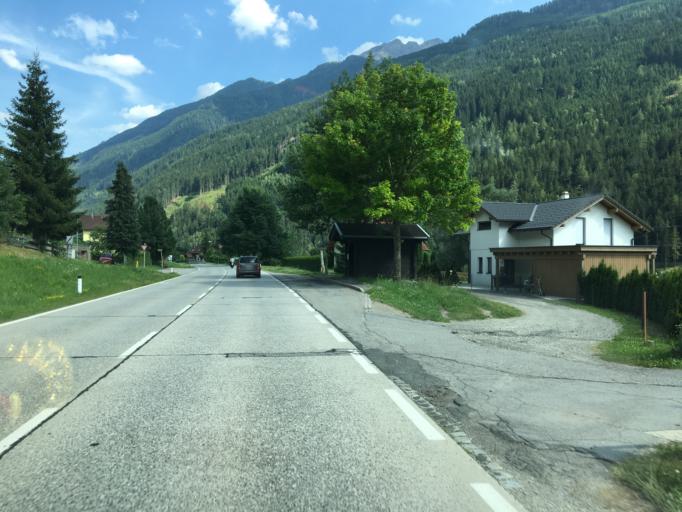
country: AT
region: Carinthia
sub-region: Politischer Bezirk Spittal an der Drau
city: Flattach
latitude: 46.9339
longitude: 13.1134
